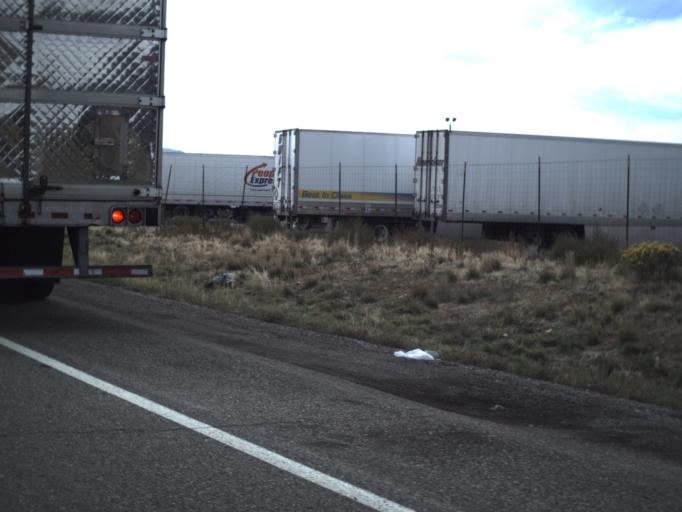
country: US
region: Utah
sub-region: Beaver County
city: Beaver
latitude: 38.2929
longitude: -112.6517
